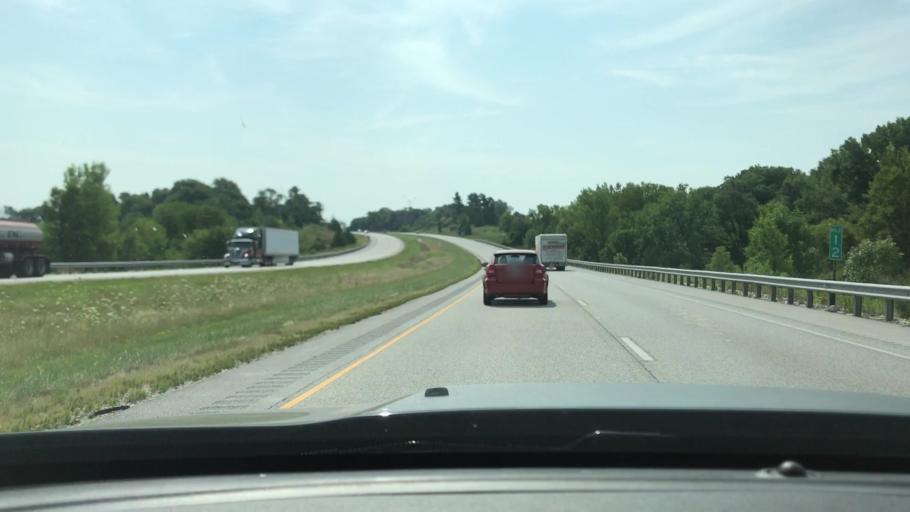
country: US
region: Illinois
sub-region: Henry County
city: Green Rock
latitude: 41.4449
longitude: -90.3656
